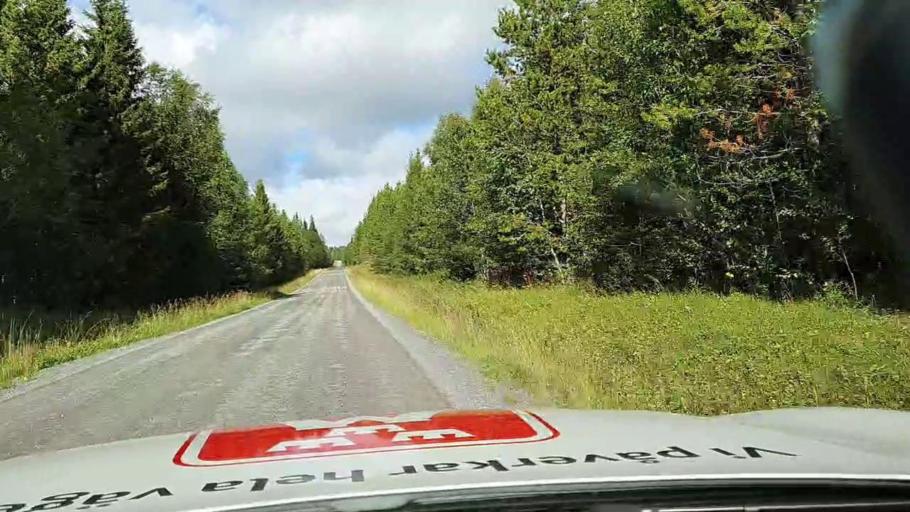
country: SE
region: Jaemtland
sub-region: Stroemsunds Kommun
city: Stroemsund
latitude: 63.7641
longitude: 15.2346
